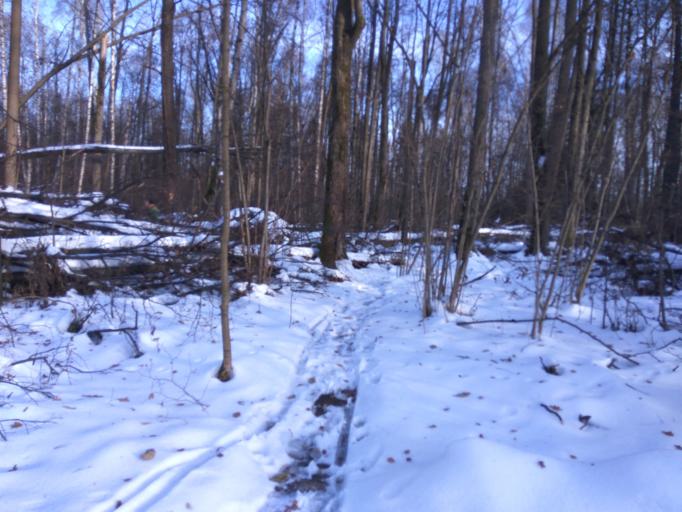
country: RU
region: Moscow
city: Babushkin
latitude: 55.8495
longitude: 37.7440
